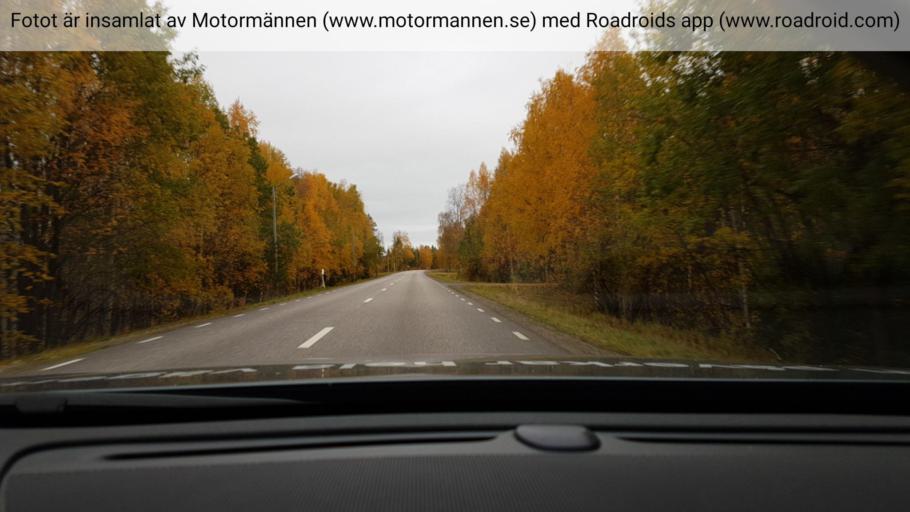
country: SE
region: Norrbotten
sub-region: Overkalix Kommun
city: OEverkalix
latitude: 66.5009
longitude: 22.7687
